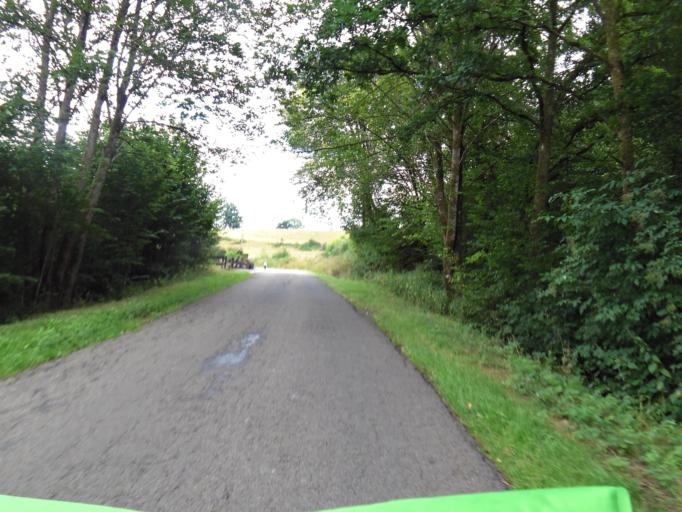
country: BE
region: Wallonia
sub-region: Province de Namur
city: Bievre
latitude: 49.8948
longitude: 5.0015
